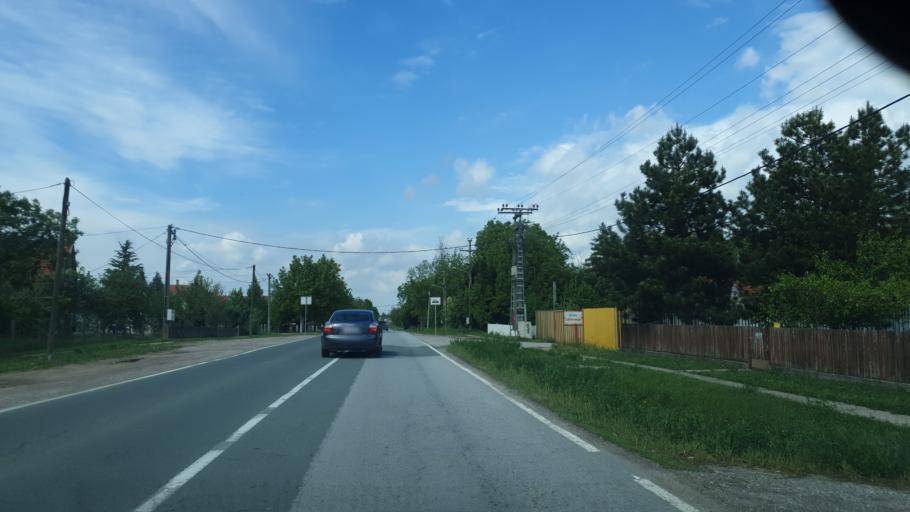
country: RS
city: Stubline
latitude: 44.5660
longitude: 20.1485
